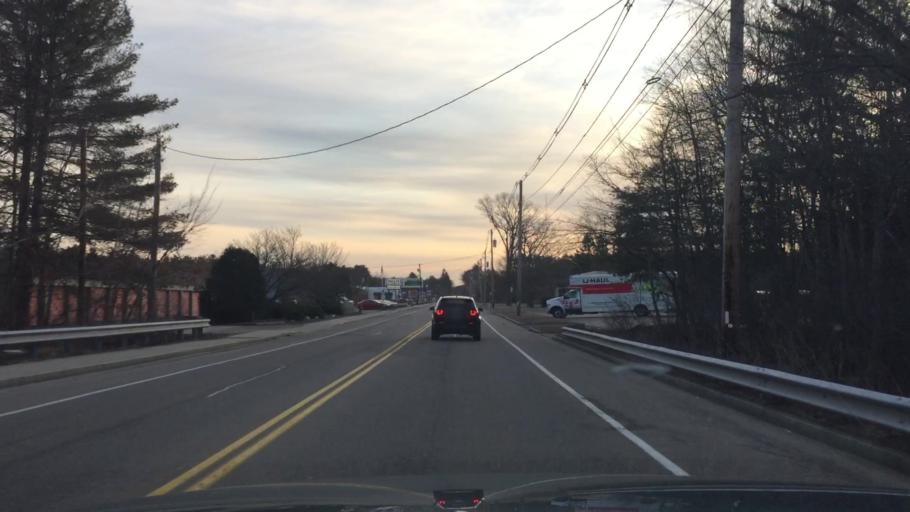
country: US
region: Massachusetts
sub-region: Norfolk County
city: Medway
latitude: 42.1579
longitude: -71.3867
